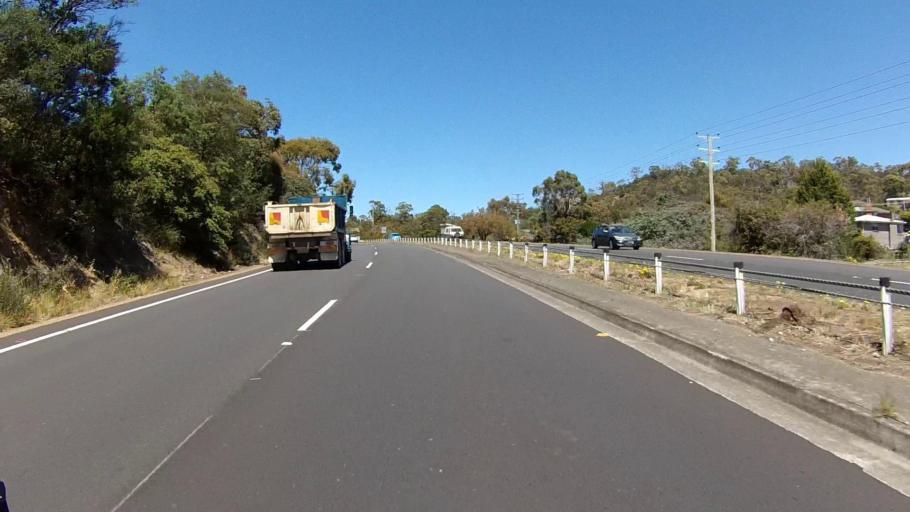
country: AU
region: Tasmania
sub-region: Clarence
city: Warrane
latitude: -42.8625
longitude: 147.3933
